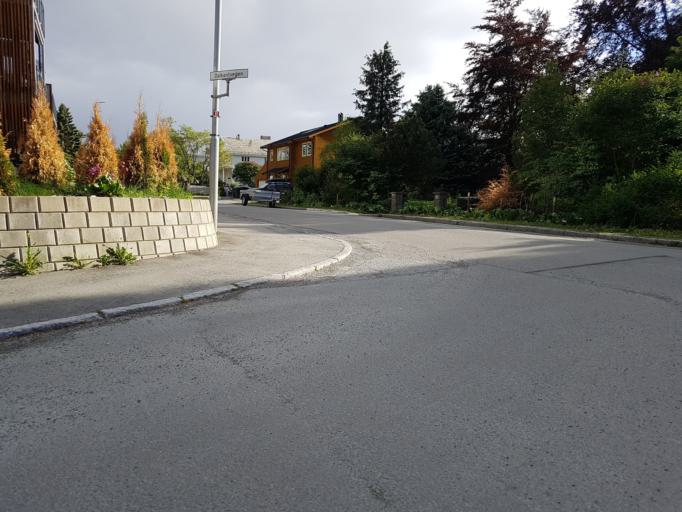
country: NO
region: Sor-Trondelag
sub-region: Trondheim
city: Trondheim
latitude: 63.4306
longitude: 10.4609
